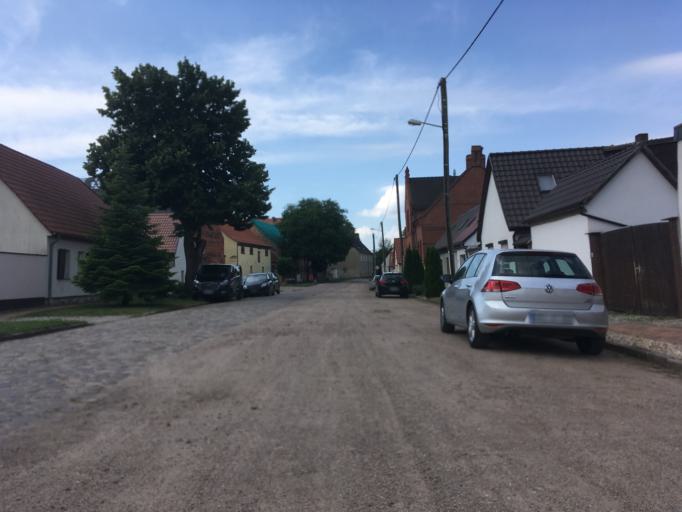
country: DE
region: Saxony-Anhalt
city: Quellendorf
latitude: 51.7691
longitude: 12.0808
